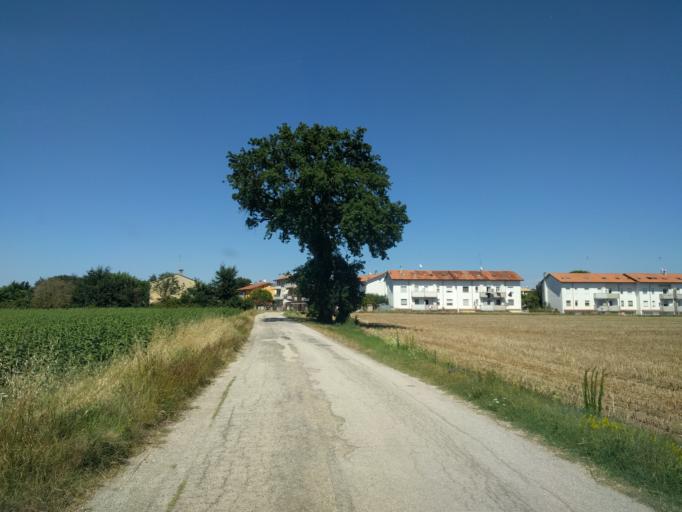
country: IT
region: The Marches
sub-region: Provincia di Pesaro e Urbino
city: Bellocchi
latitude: 43.7981
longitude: 12.9912
